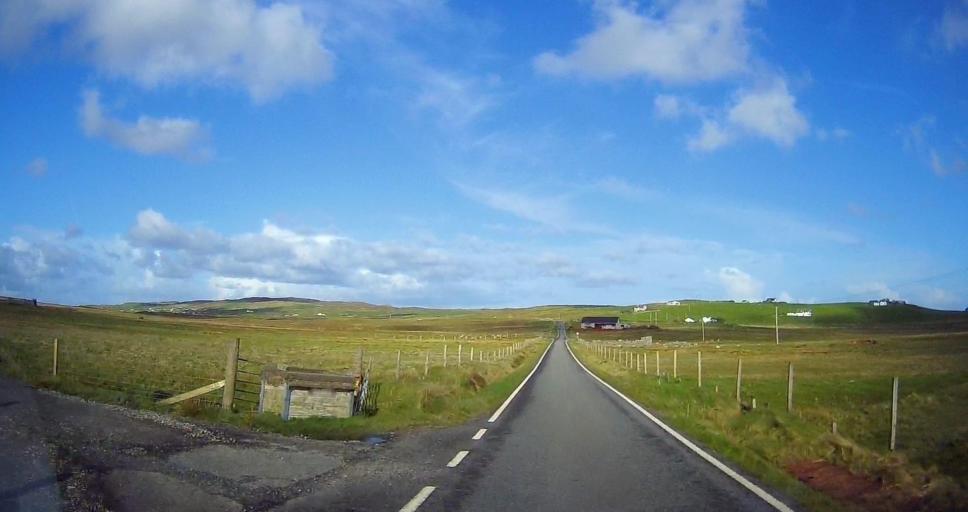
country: GB
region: Scotland
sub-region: Shetland Islands
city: Shetland
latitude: 60.3560
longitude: -1.1583
